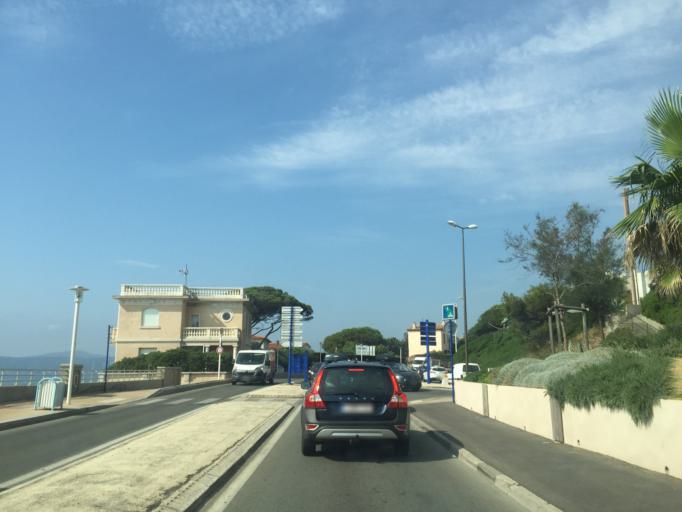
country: FR
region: Provence-Alpes-Cote d'Azur
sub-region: Departement du Var
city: Sainte-Maxime
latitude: 43.3060
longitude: 6.6325
